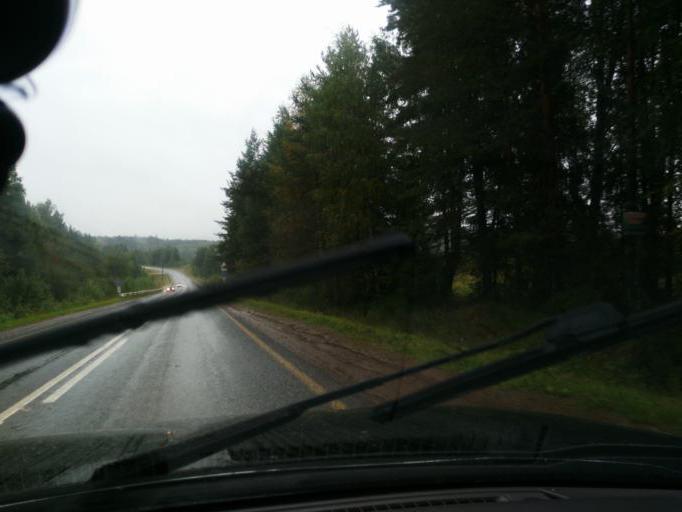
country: RU
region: Perm
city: Yugo-Kamskiy
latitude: 57.5688
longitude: 55.6814
